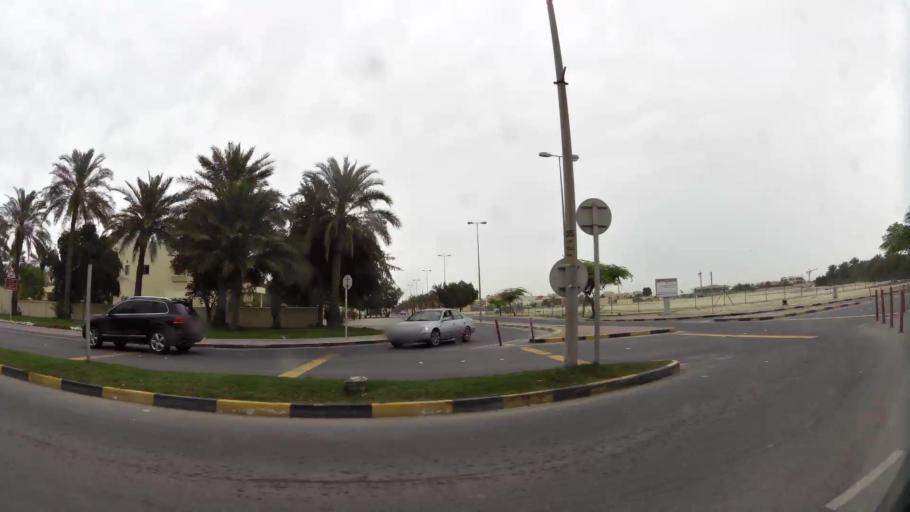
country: BH
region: Northern
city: Ar Rifa'
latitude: 26.1196
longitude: 50.5368
